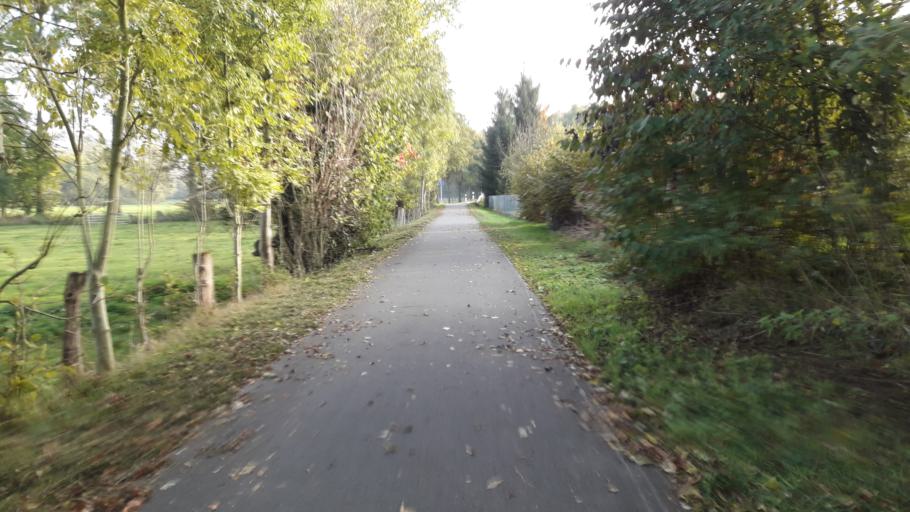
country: DE
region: North Rhine-Westphalia
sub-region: Regierungsbezirk Detmold
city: Paderborn
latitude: 51.6808
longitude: 8.6986
